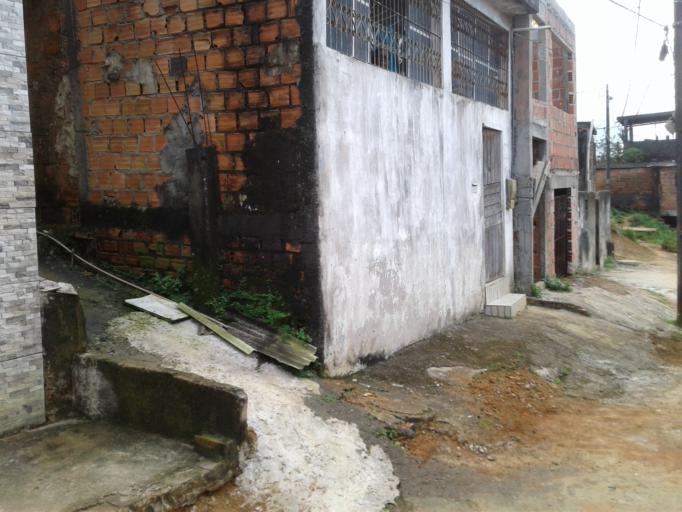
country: BR
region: Bahia
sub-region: Salvador
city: Salvador
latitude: -12.9105
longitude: -38.4730
